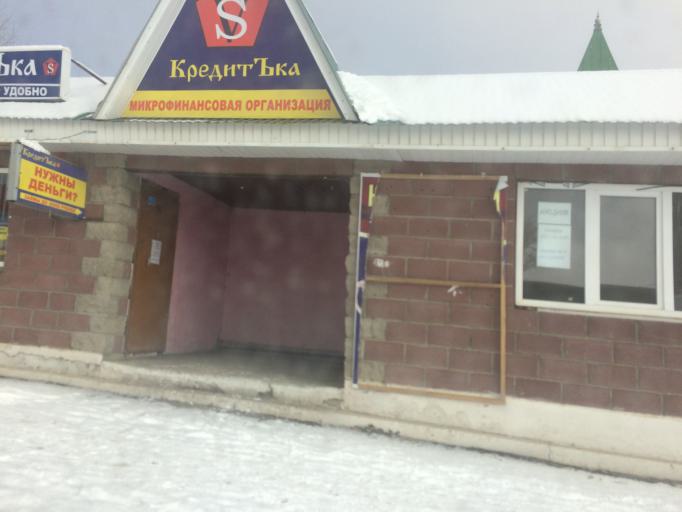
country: RU
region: Bashkortostan
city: Abzakovo
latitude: 53.3365
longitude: 58.5073
